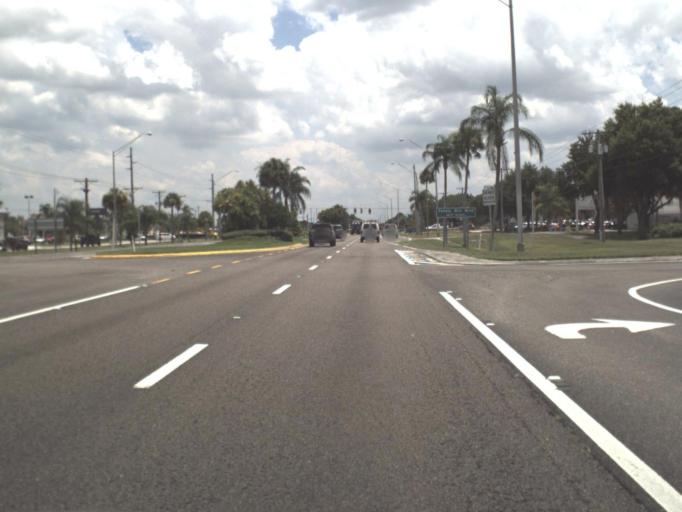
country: US
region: Florida
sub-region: Hillsborough County
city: Sun City Center
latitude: 27.7122
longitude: -82.3543
